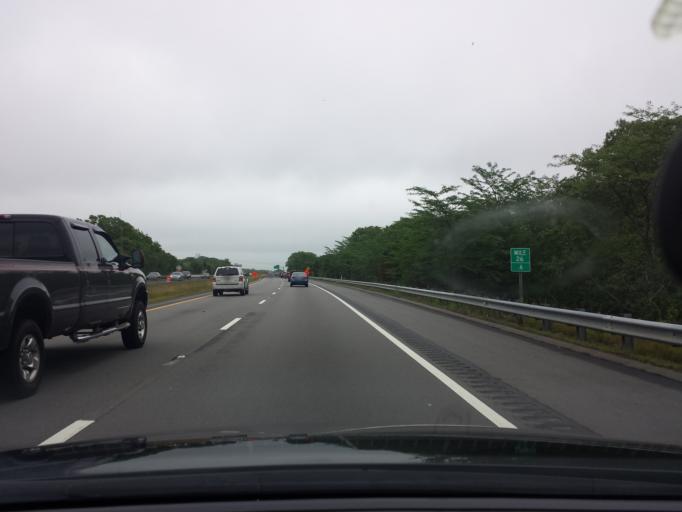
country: US
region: Massachusetts
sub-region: Bristol County
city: Fairhaven
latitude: 41.6552
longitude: -70.8996
